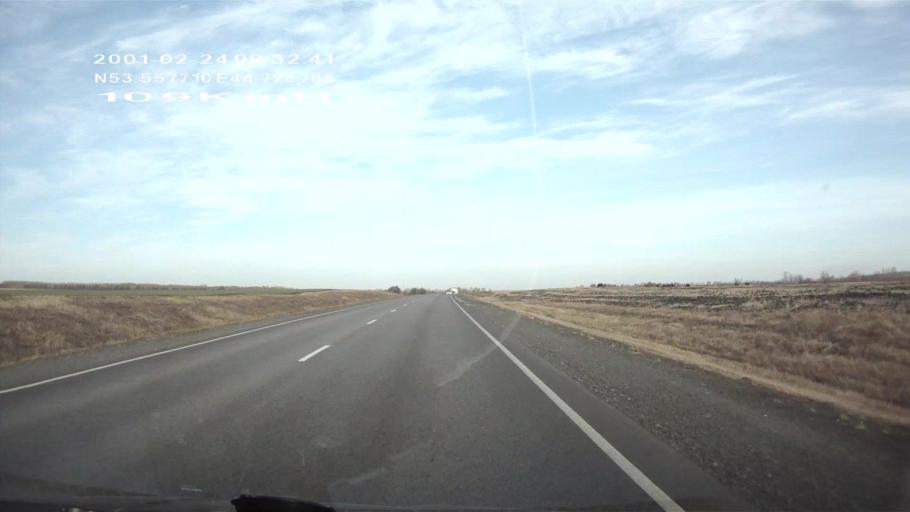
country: RU
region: Penza
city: Mokshan
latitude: 53.5578
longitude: 44.7267
